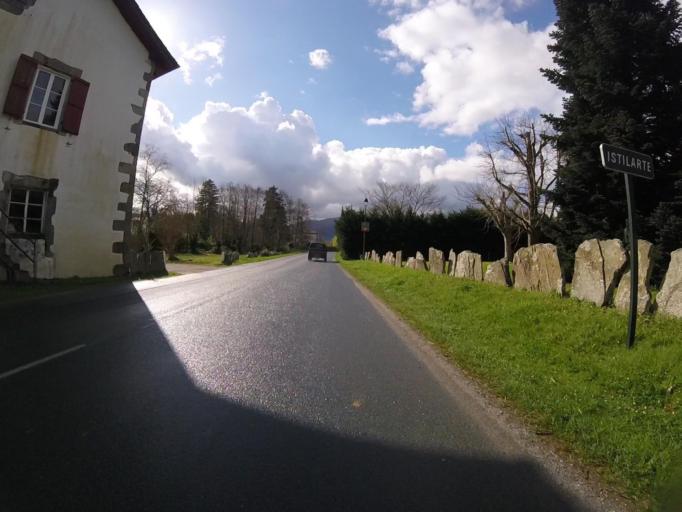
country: FR
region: Aquitaine
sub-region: Departement des Pyrenees-Atlantiques
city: Sare
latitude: 43.3085
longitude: -1.5727
